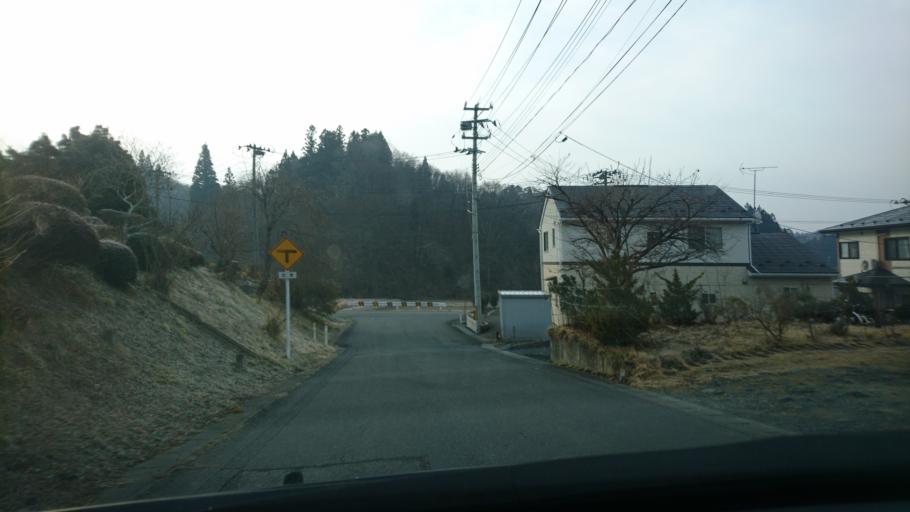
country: JP
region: Iwate
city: Ichinoseki
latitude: 38.9112
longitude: 141.3410
